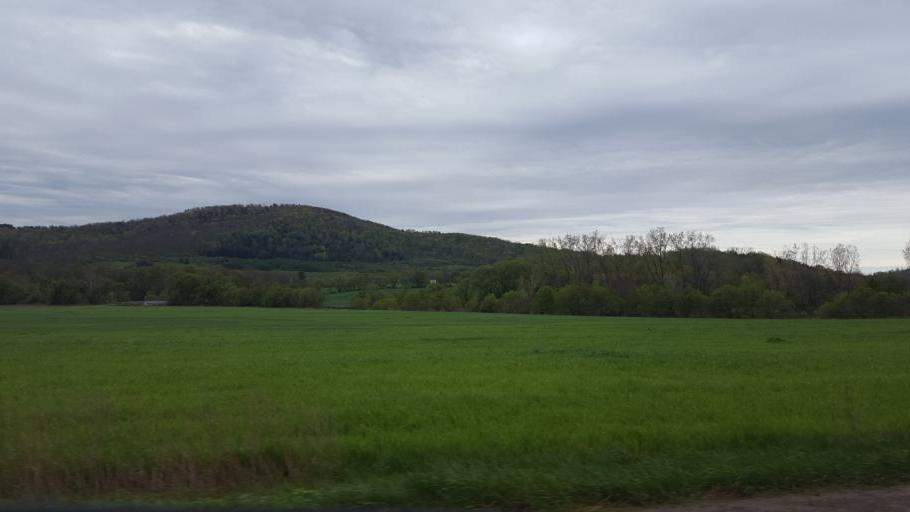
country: US
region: Pennsylvania
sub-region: Tioga County
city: Westfield
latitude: 41.9531
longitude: -77.4623
